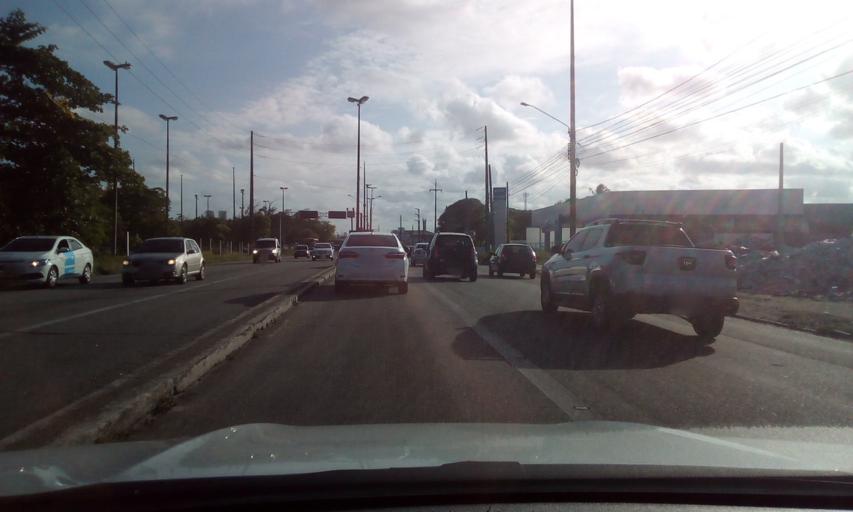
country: BR
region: Pernambuco
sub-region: Olinda
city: Olinda
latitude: -8.0245
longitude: -34.8629
